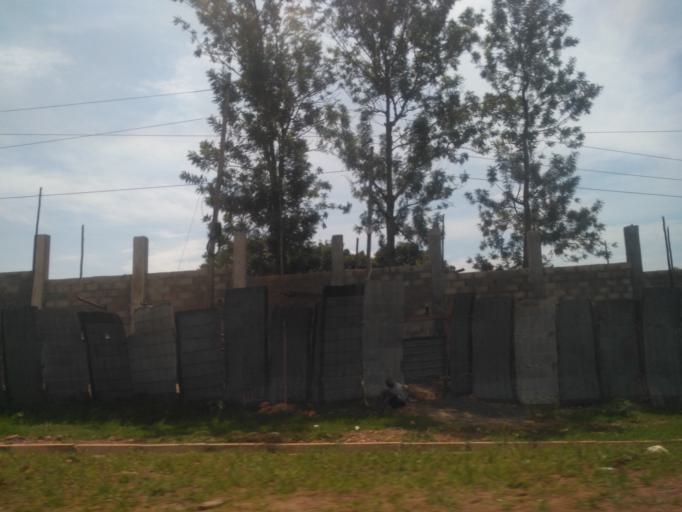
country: UG
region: Central Region
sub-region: Wakiso District
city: Entebbe
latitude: 0.0891
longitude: 32.4895
